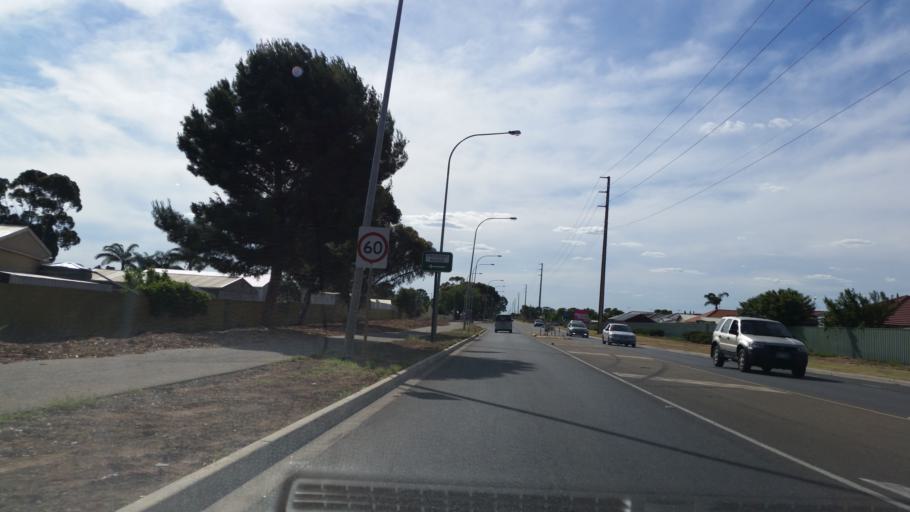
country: AU
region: South Australia
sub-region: Playford
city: Smithfield
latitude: -34.6679
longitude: 138.6699
